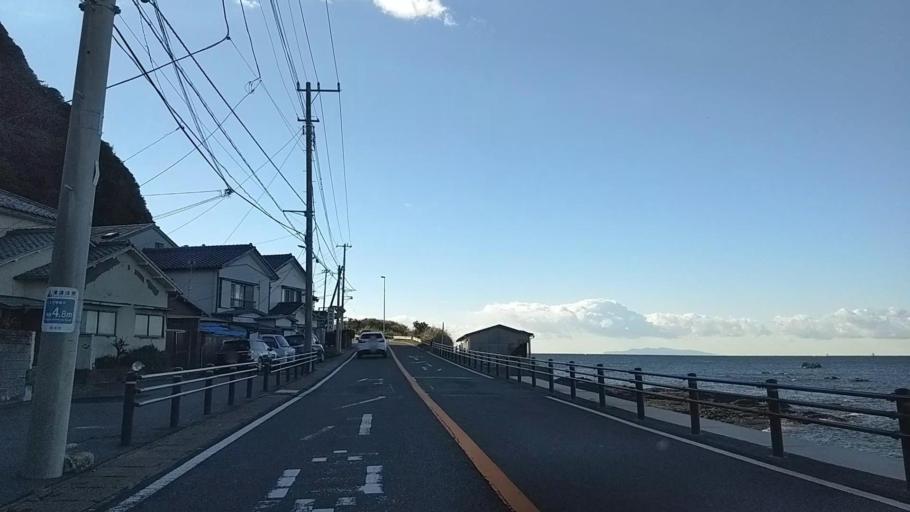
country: JP
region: Chiba
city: Futtsu
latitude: 35.1622
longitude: 139.8199
